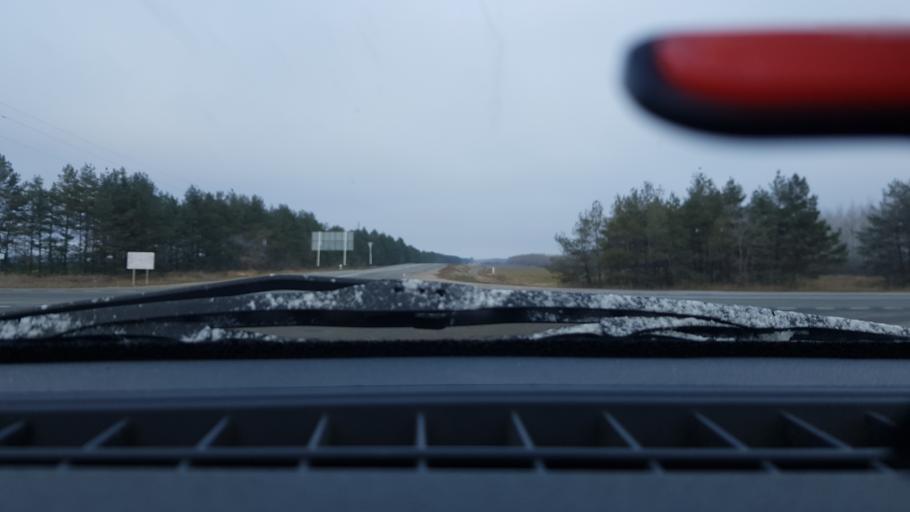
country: RU
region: Tatarstan
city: Kuybyshevskiy Zaton
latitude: 54.9465
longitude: 49.4491
